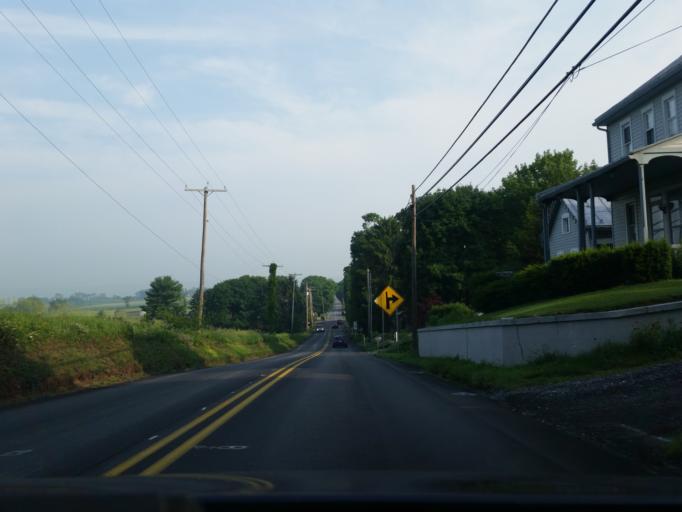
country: US
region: Pennsylvania
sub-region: Lebanon County
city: Annville
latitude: 40.3654
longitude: -76.5476
